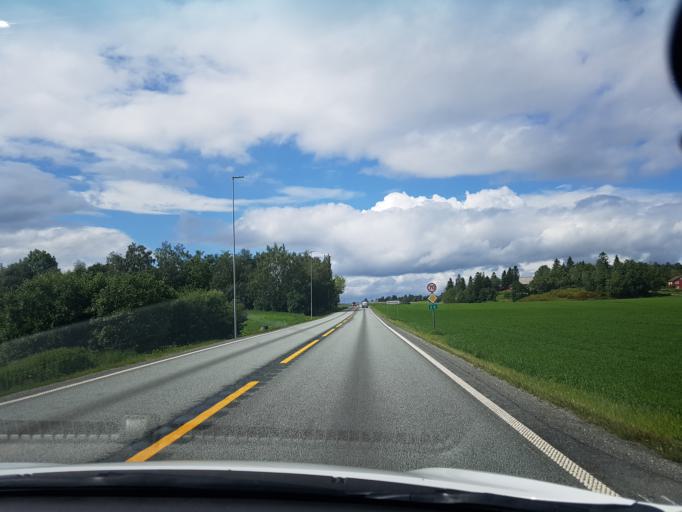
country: NO
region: Nord-Trondelag
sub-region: Stjordal
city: Stjordal
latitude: 63.5200
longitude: 10.8548
